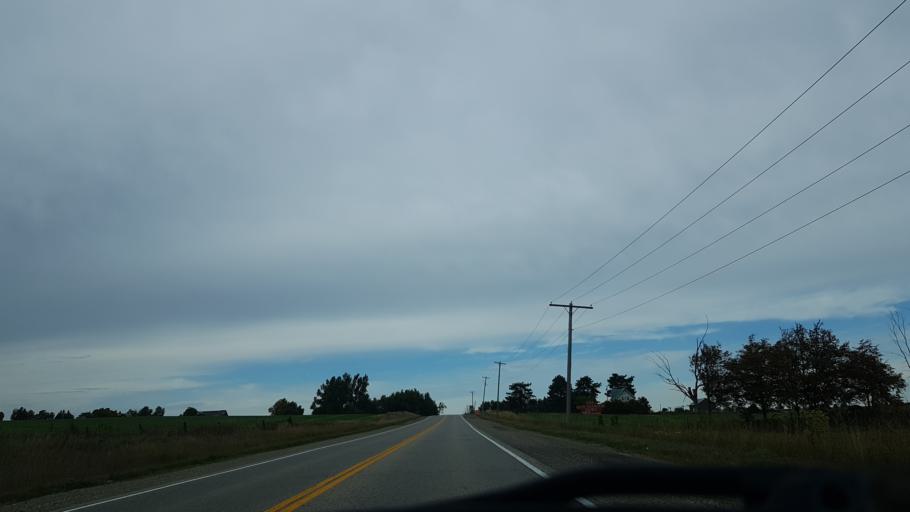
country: CA
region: Ontario
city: Shelburne
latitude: 44.1309
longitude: -80.0289
